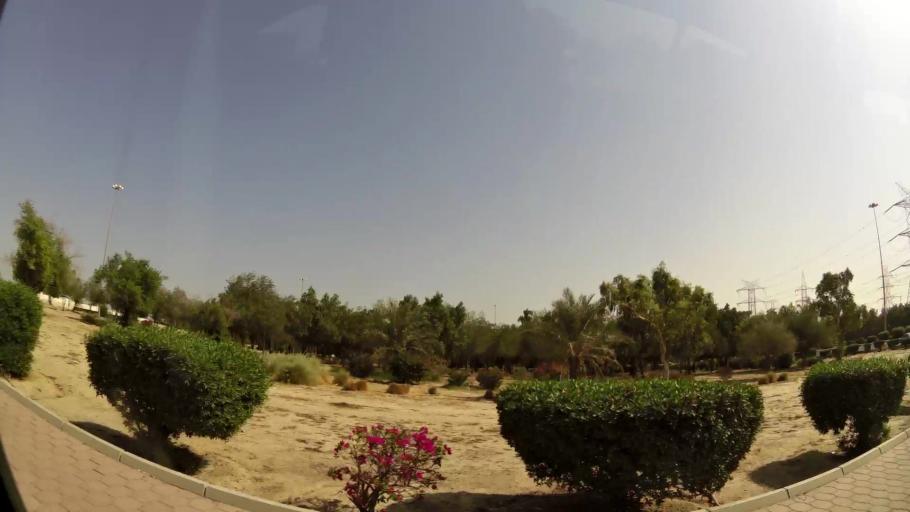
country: KW
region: Mubarak al Kabir
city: Sabah as Salim
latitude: 29.2642
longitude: 48.0408
